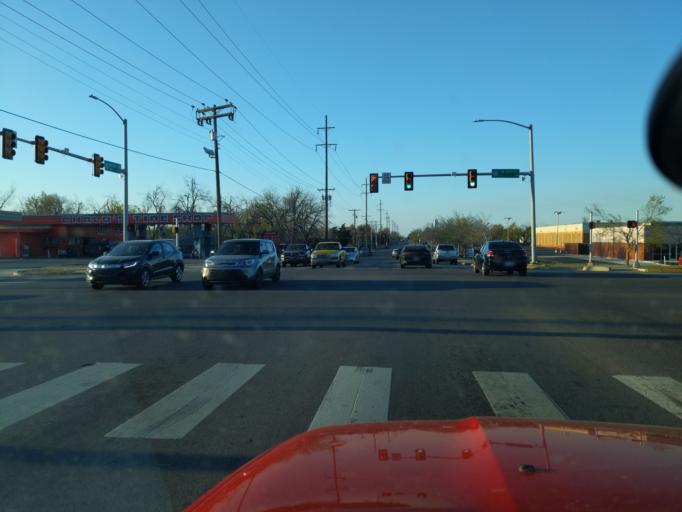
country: US
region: Oklahoma
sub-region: Oklahoma County
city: Oklahoma City
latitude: 35.4061
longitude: -97.5213
